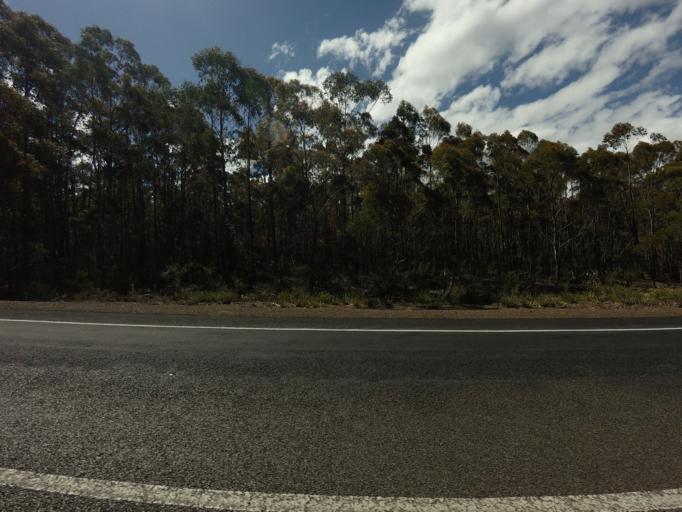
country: AU
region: Tasmania
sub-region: Northern Midlands
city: Evandale
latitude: -42.0131
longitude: 147.8684
